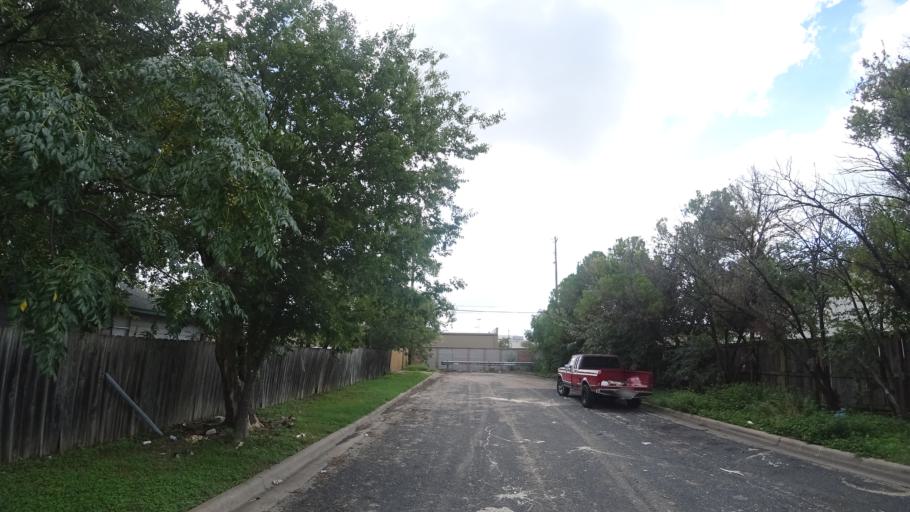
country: US
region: Texas
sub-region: Travis County
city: Austin
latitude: 30.3518
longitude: -97.7172
